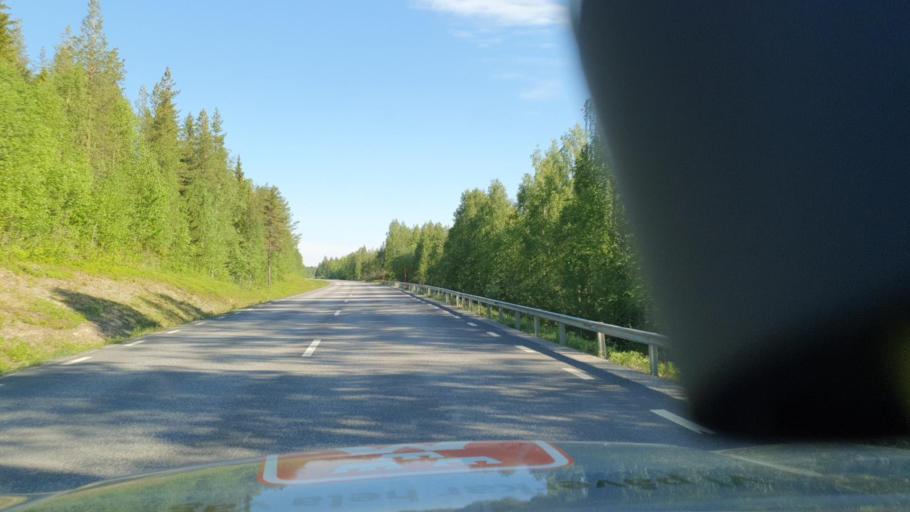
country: SE
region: Norrbotten
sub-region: Alvsbyns Kommun
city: AElvsbyn
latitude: 66.2688
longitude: 20.8307
